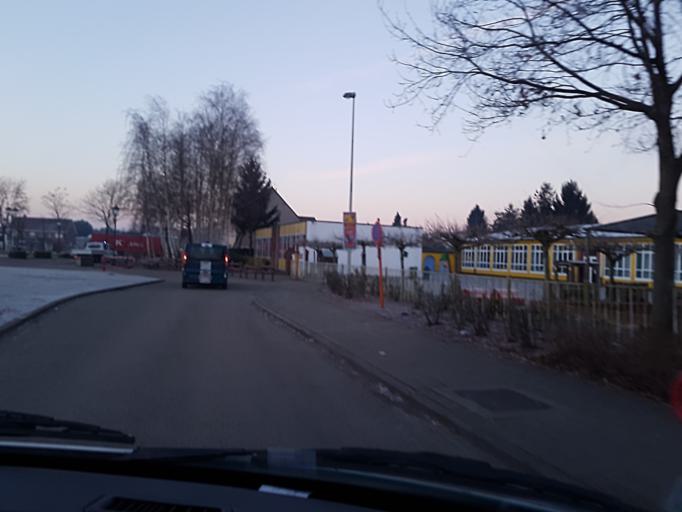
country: BE
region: Flanders
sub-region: Provincie Antwerpen
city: Schilde
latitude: 51.2653
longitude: 4.6334
